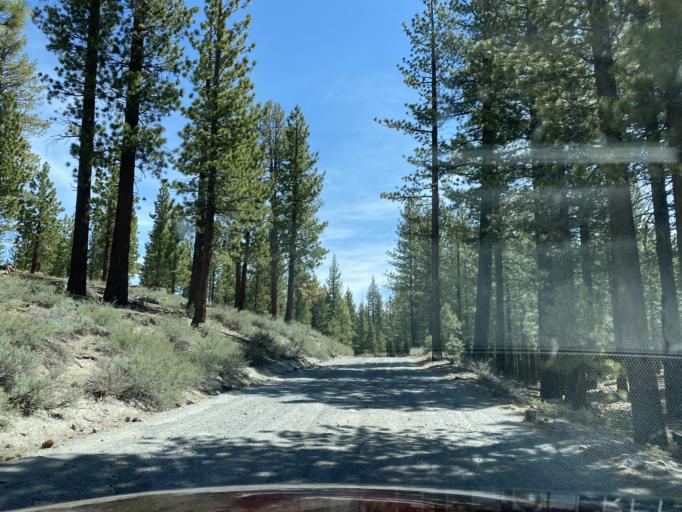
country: US
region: California
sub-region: Mono County
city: Mammoth Lakes
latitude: 37.7681
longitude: -119.0230
